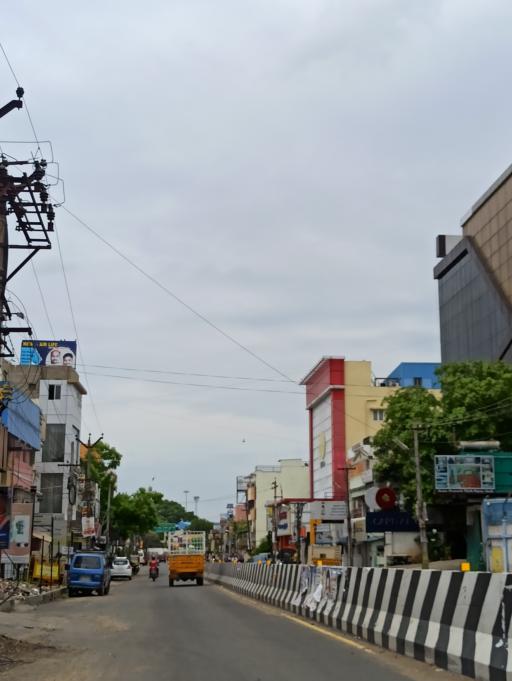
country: IN
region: Tamil Nadu
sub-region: Kancheepuram
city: Pallavaram
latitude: 12.9305
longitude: 80.1182
